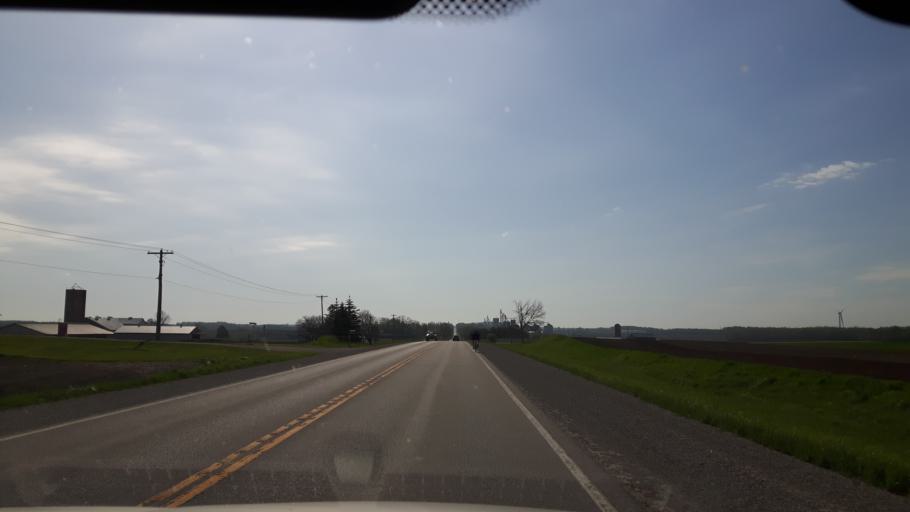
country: CA
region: Ontario
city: Bluewater
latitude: 43.5411
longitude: -81.6277
